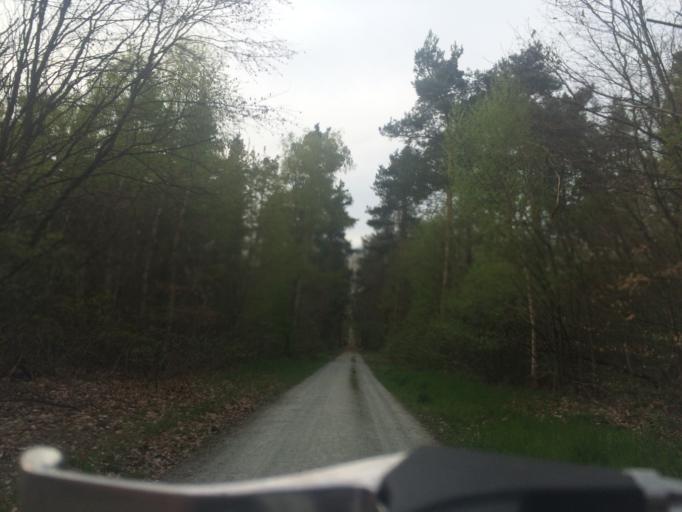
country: DE
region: Hesse
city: Morfelden-Walldorf
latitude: 50.0080
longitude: 8.5914
